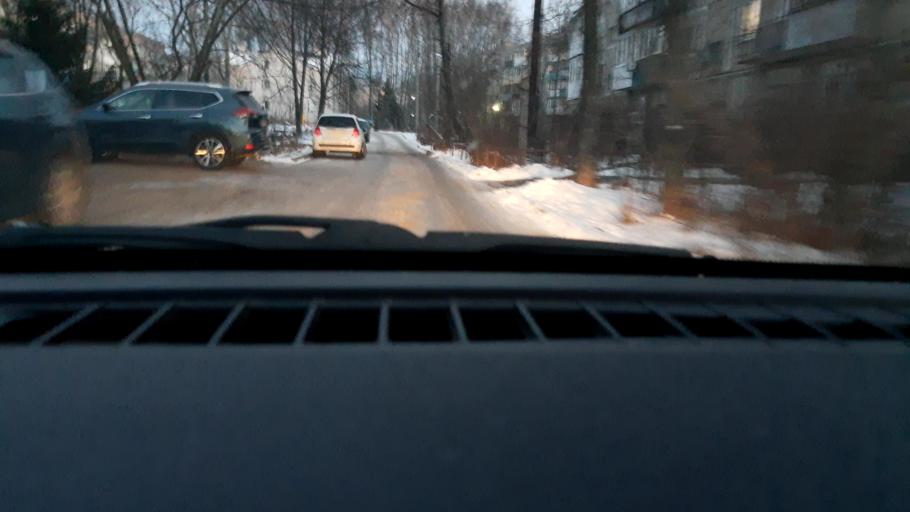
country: RU
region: Nizjnij Novgorod
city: Afonino
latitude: 56.2087
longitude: 44.0270
